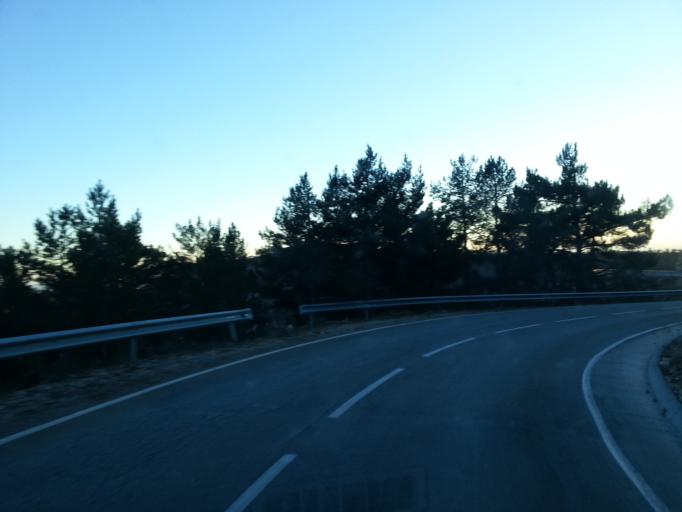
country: ES
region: Catalonia
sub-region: Provincia de Lleida
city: Olius
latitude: 42.1448
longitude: 1.5532
